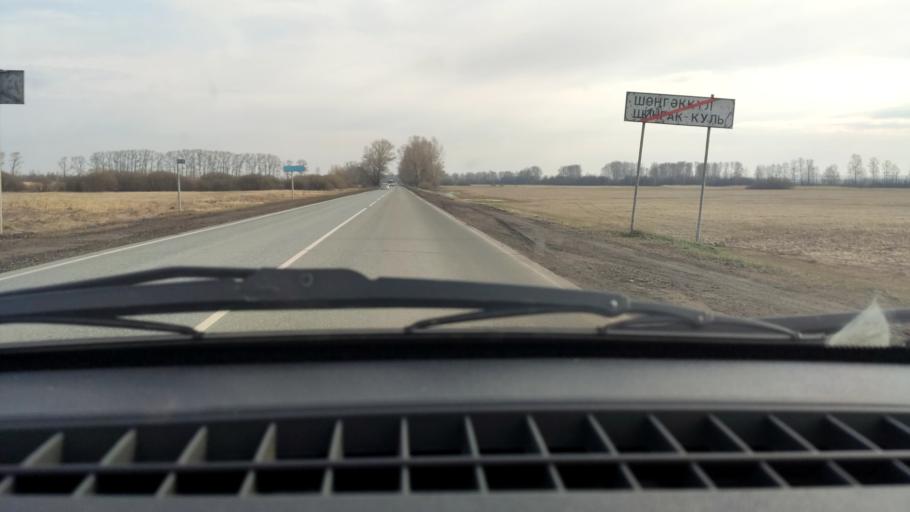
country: RU
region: Bashkortostan
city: Chishmy
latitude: 54.3985
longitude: 55.2104
